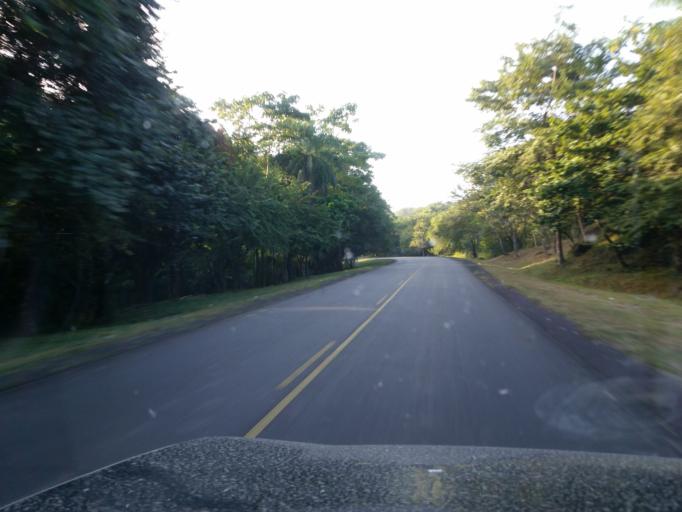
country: NI
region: Rio San Juan
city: El Almendro
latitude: 11.5734
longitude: -84.8291
